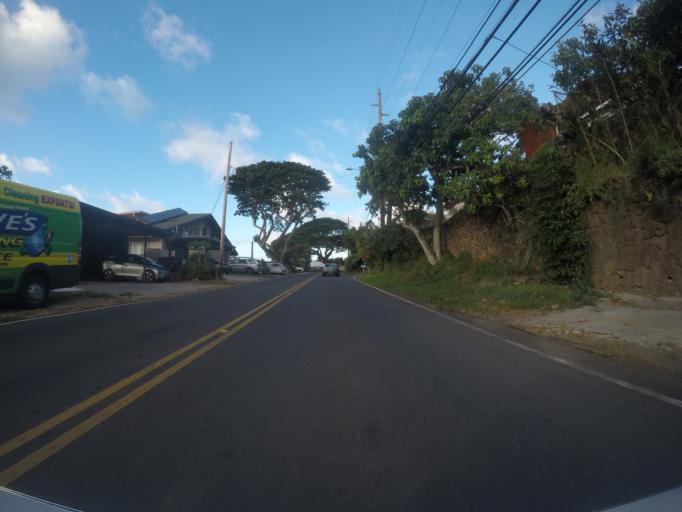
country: US
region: Hawaii
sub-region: Honolulu County
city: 'Ahuimanu
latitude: 21.4537
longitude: -157.8178
